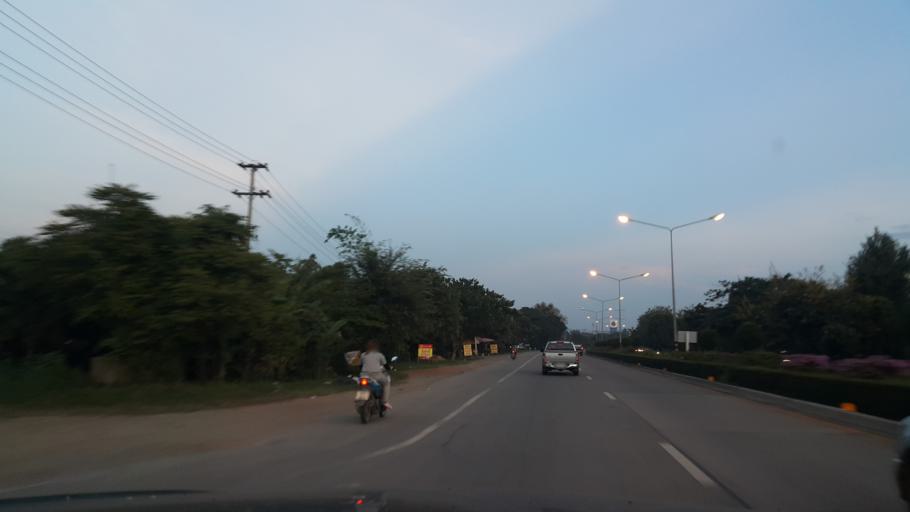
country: TH
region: Lamphun
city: Lamphun
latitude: 18.5692
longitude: 99.0232
